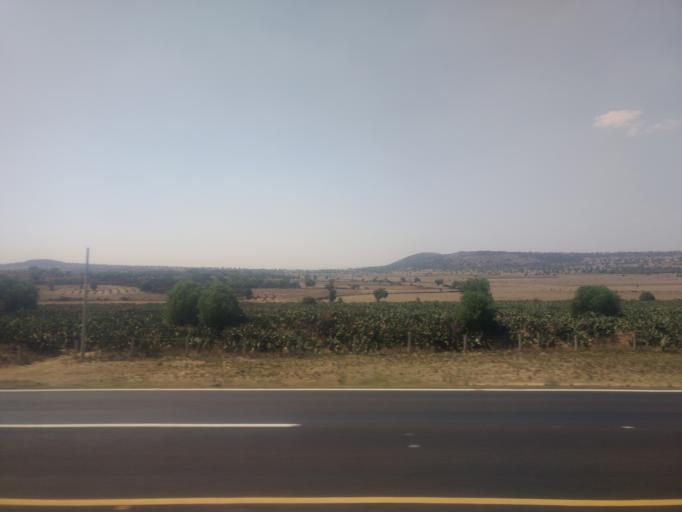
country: MX
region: Morelos
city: Nopaltepec
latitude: 19.8143
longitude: -98.7163
